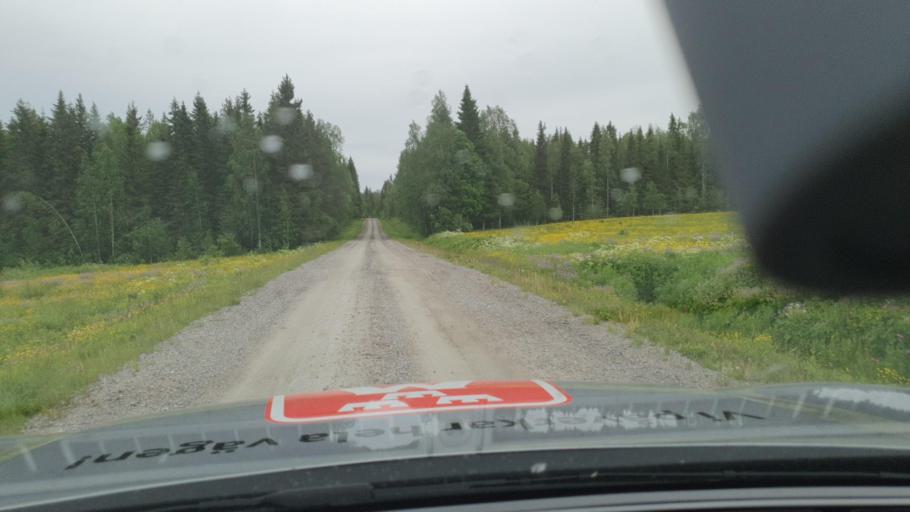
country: SE
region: Norrbotten
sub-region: Overkalix Kommun
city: OEverkalix
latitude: 66.0805
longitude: 22.9111
